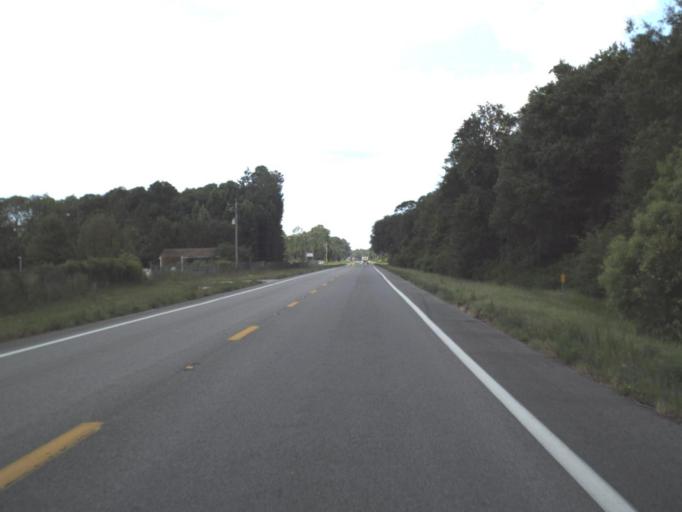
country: US
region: Florida
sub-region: Taylor County
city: Perry
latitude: 30.0914
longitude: -83.6428
